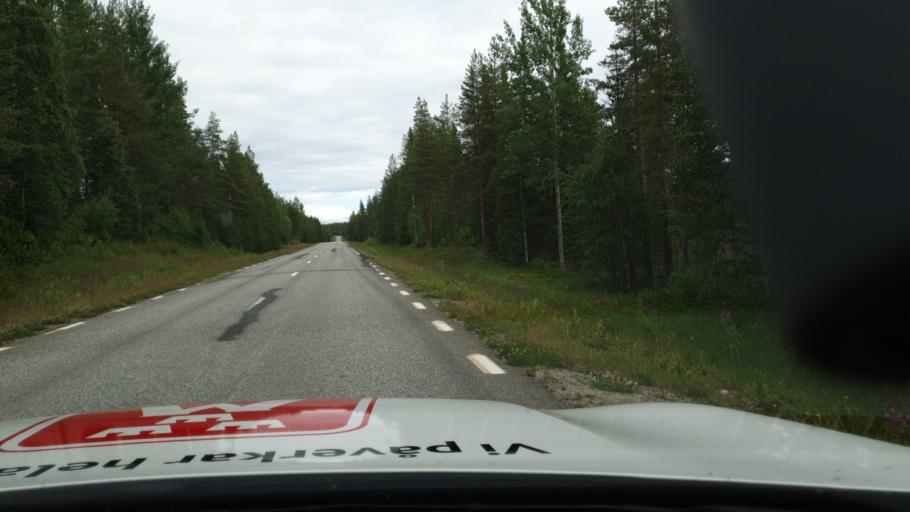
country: SE
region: Vaesterbotten
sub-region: Lycksele Kommun
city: Soderfors
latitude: 64.6194
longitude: 18.1512
